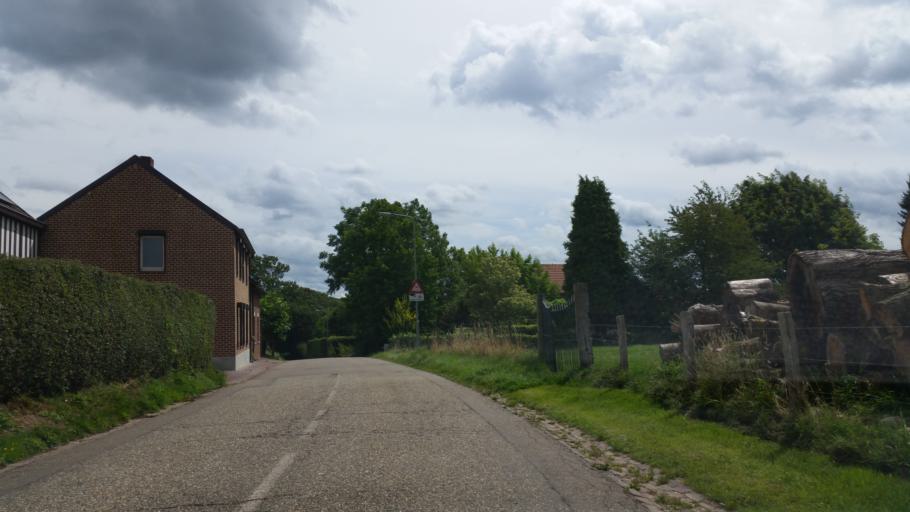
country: NL
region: Limburg
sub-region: Eijsden-Margraten
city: Margraten
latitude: 50.8314
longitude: 5.7974
